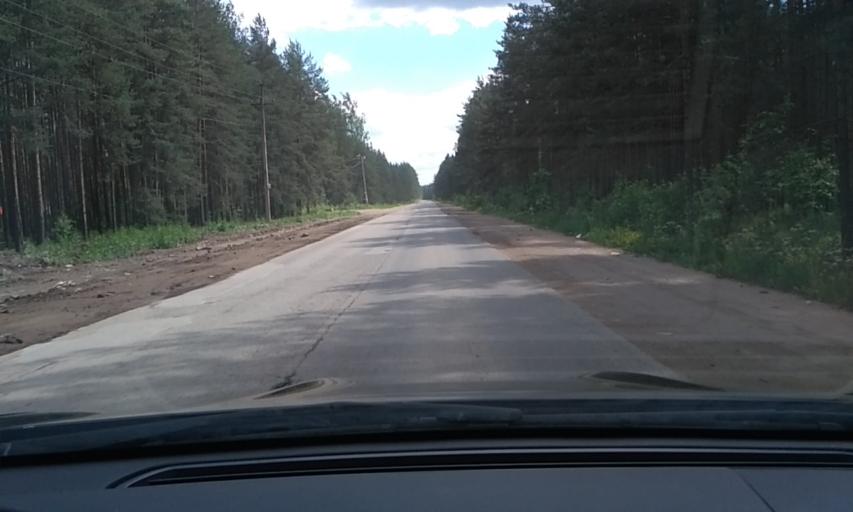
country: RU
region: Leningrad
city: Imeni Sverdlova
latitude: 59.8505
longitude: 30.6803
